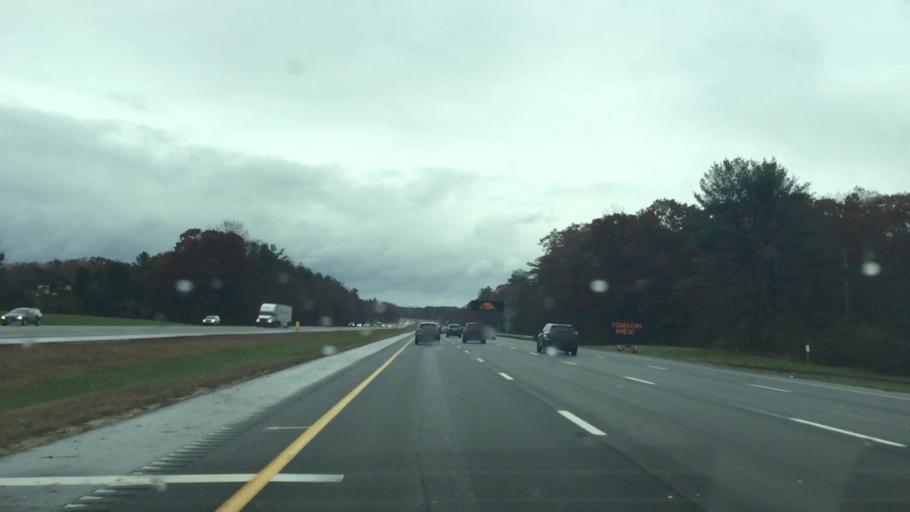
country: US
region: New Hampshire
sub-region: Rockingham County
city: Hampton Falls
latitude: 42.9212
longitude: -70.8692
